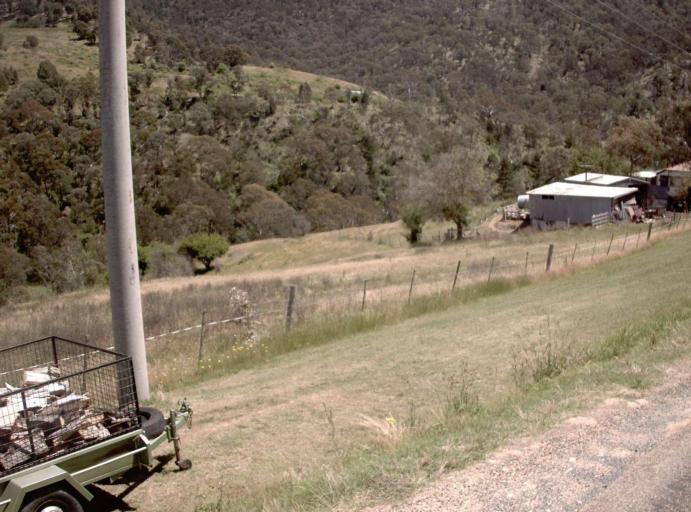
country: AU
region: Victoria
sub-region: Alpine
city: Mount Beauty
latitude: -37.1050
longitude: 147.5818
